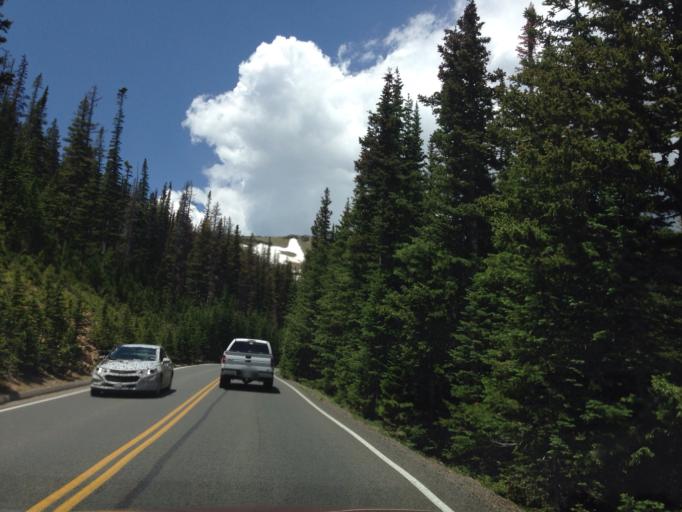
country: US
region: Colorado
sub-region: Larimer County
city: Estes Park
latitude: 40.3873
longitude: -105.6689
